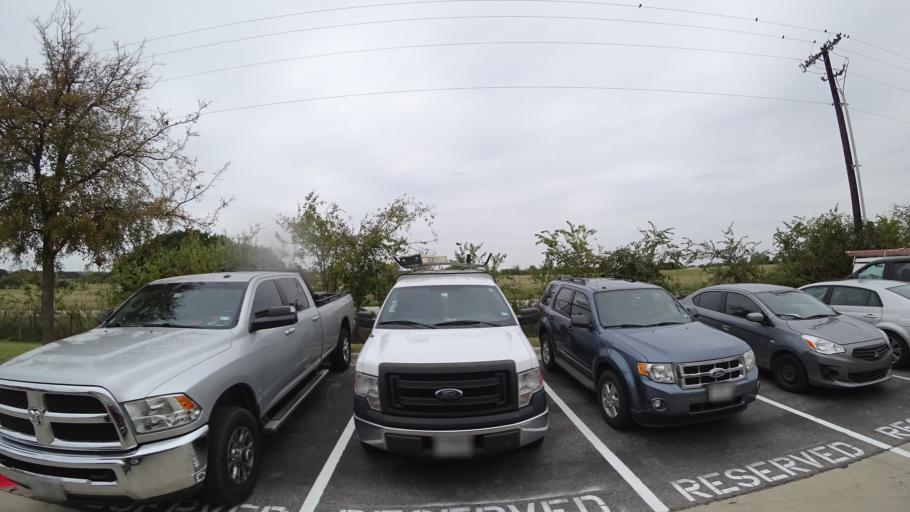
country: US
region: Texas
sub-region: Travis County
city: Wells Branch
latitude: 30.4488
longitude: -97.7090
